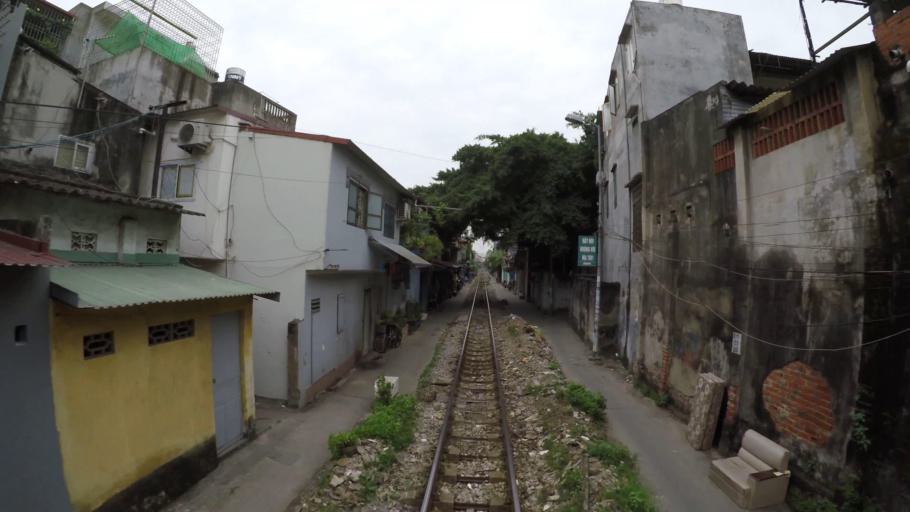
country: VN
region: Hai Phong
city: Haiphong
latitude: 20.8592
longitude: 106.6638
